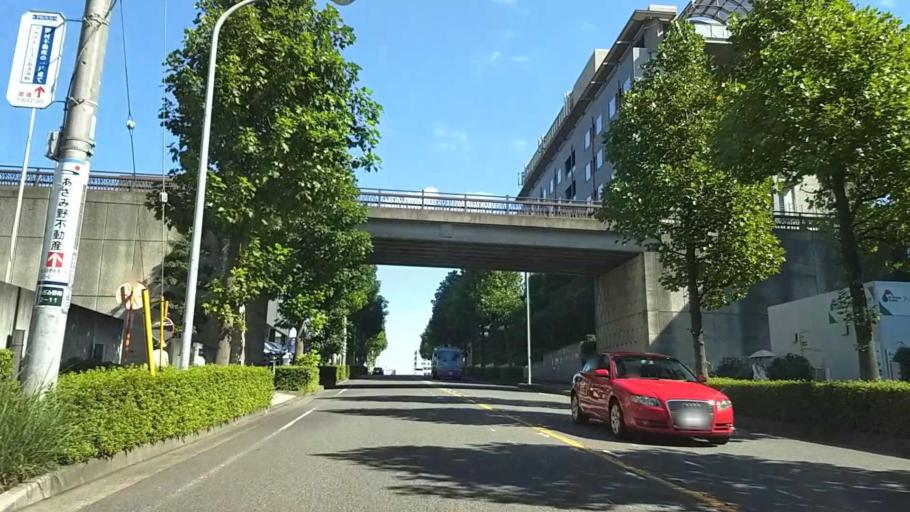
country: JP
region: Tokyo
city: Chofugaoka
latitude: 35.5651
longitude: 139.5536
